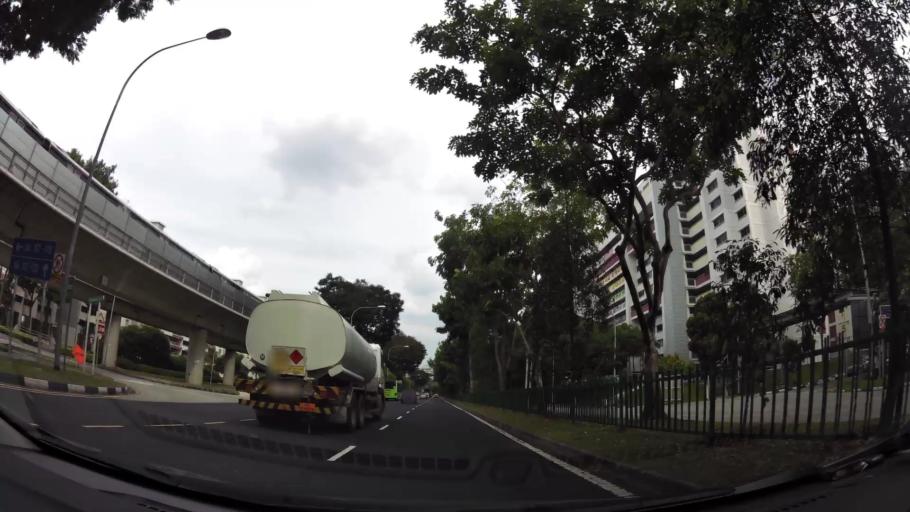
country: MY
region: Johor
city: Johor Bahru
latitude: 1.4323
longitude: 103.7754
